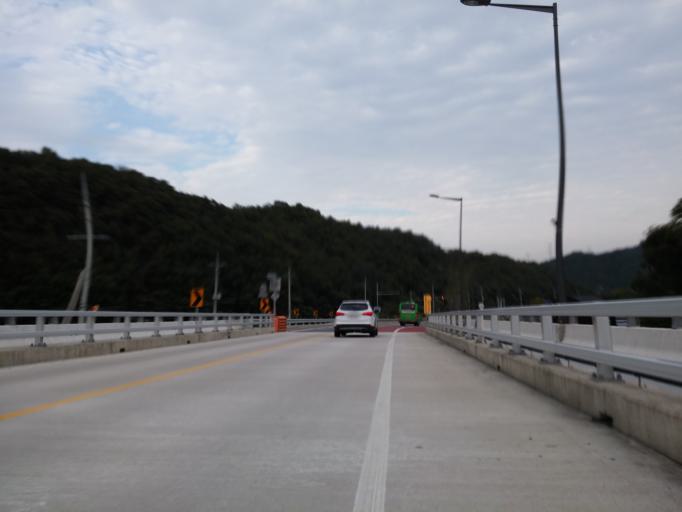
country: KR
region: Daejeon
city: Daejeon
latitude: 36.2297
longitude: 127.3034
